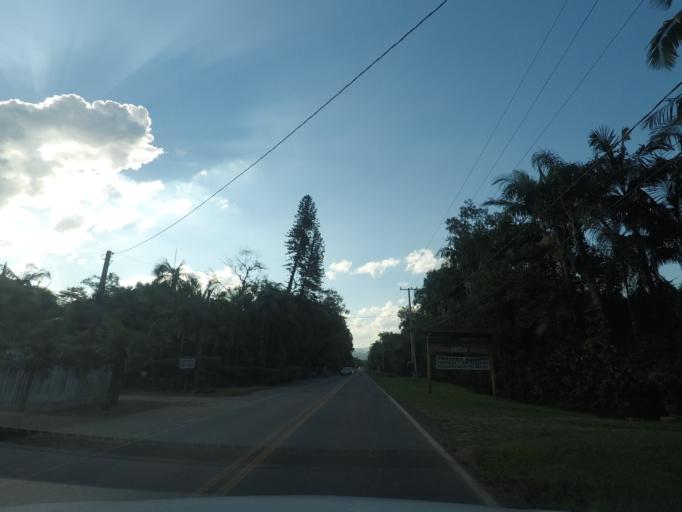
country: BR
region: Parana
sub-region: Antonina
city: Antonina
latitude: -25.4422
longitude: -48.8757
